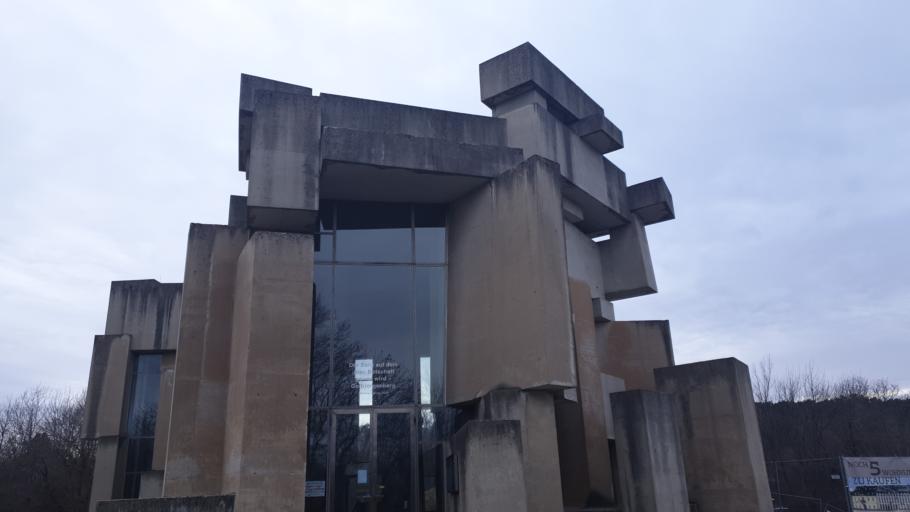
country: AT
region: Lower Austria
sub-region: Politischer Bezirk Modling
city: Perchtoldsdorf
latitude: 48.1476
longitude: 16.2538
